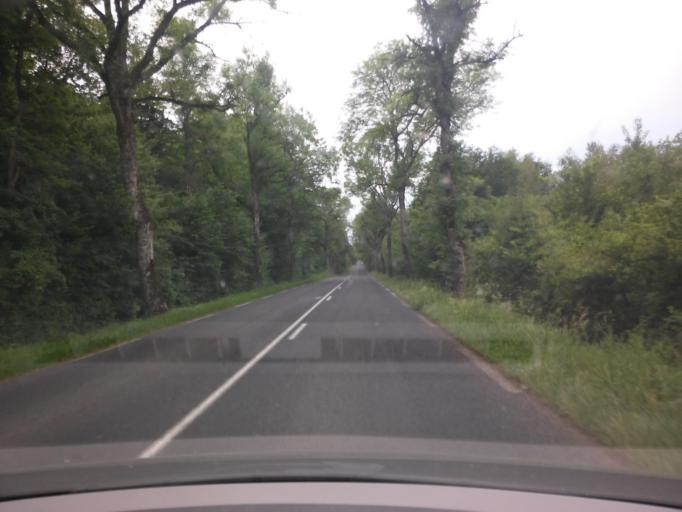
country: FR
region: Lorraine
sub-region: Departement de la Meuse
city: Vigneulles-les-Hattonchatel
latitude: 48.8670
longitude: 5.8261
